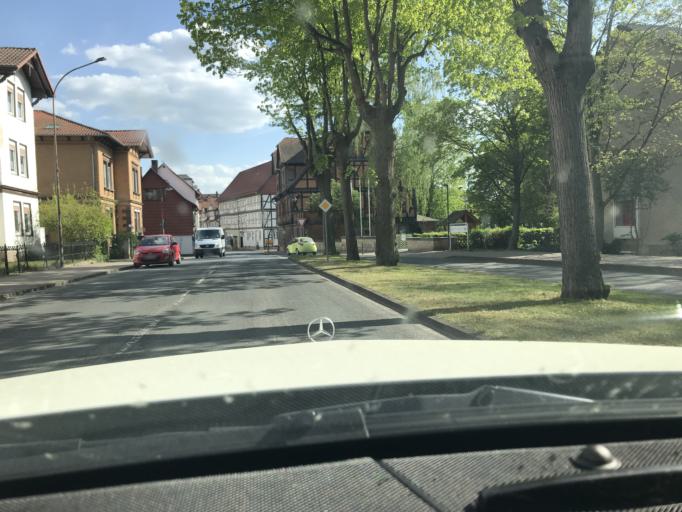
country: DE
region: Hesse
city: Wanfried
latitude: 51.1839
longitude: 10.1694
